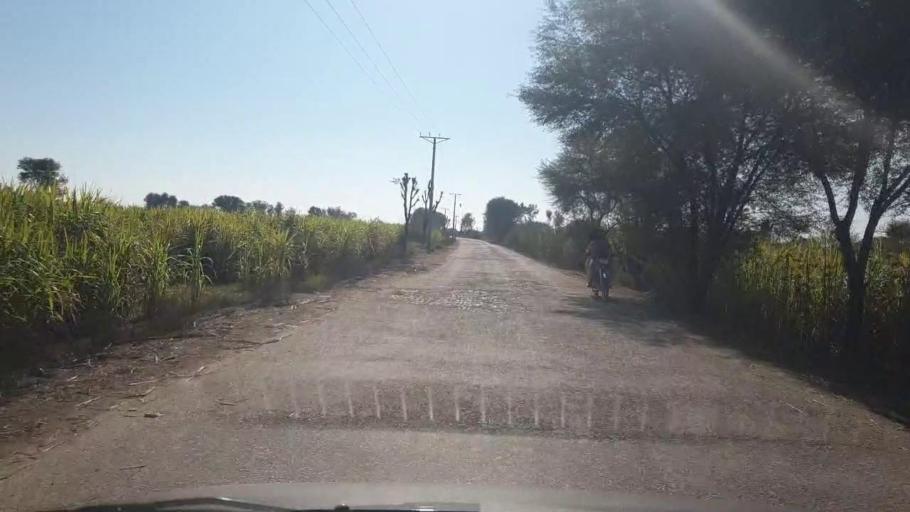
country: PK
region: Sindh
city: Bozdar
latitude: 27.2655
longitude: 68.6523
